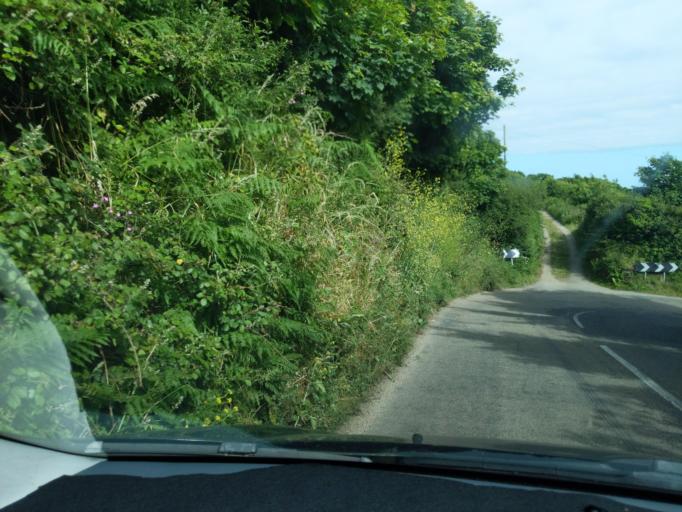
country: GB
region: England
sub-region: Cornwall
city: St. Buryan
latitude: 50.0535
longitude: -5.6362
